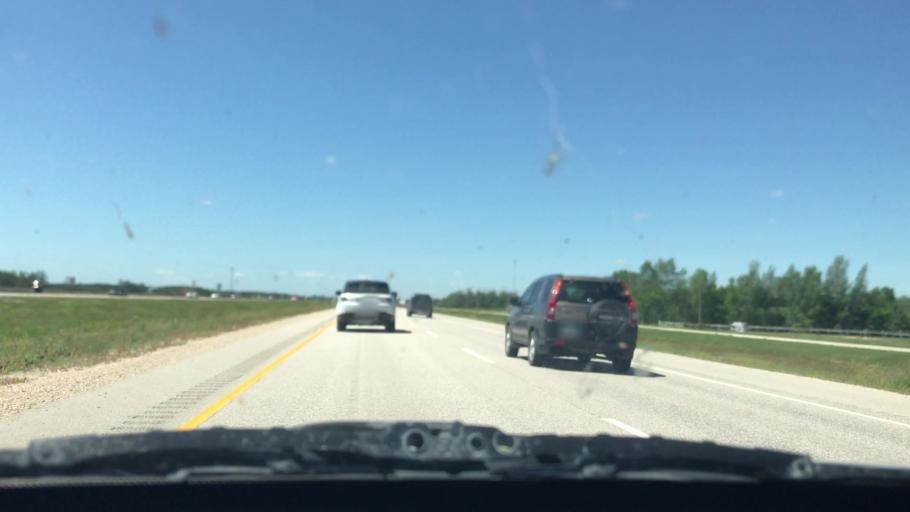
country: CA
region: Manitoba
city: Winnipeg
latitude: 49.8141
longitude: -96.9206
